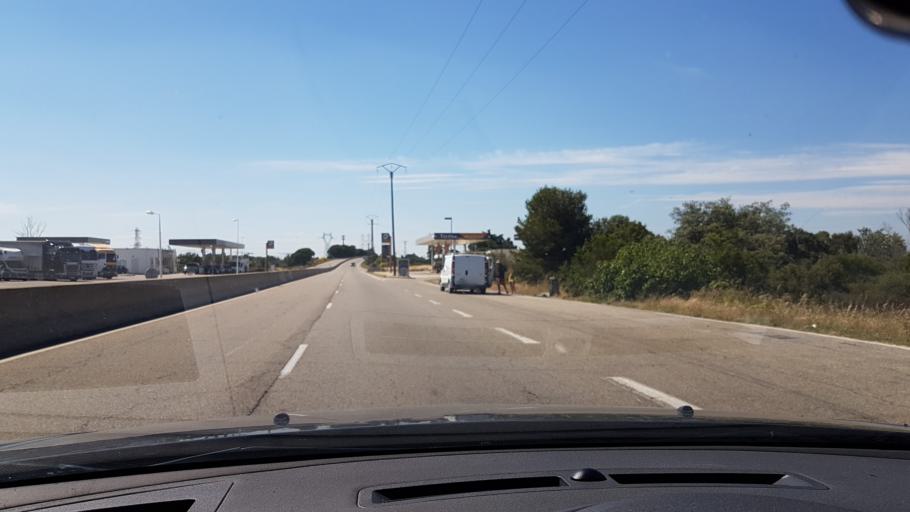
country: FR
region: Provence-Alpes-Cote d'Azur
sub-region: Departement des Bouches-du-Rhone
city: Fos-sur-Mer
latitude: 43.4705
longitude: 4.9095
